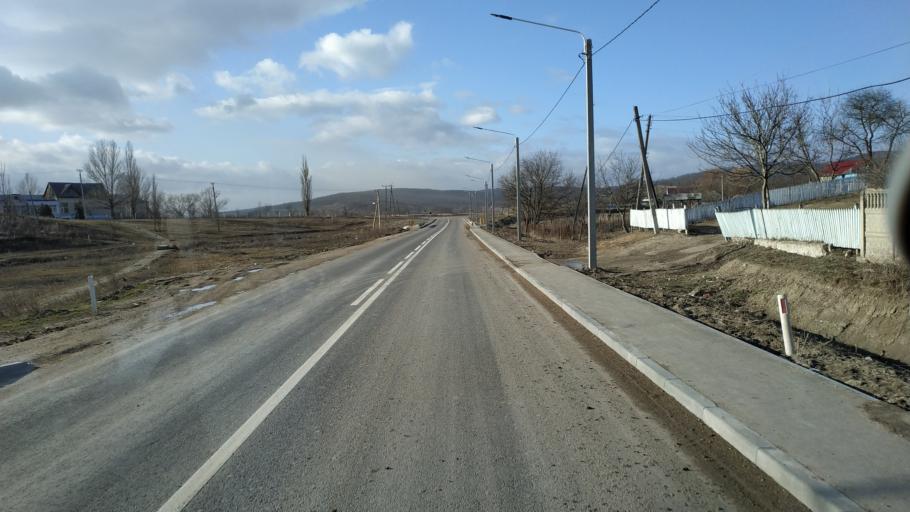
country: MD
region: Calarasi
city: Calarasi
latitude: 47.3216
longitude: 28.1079
